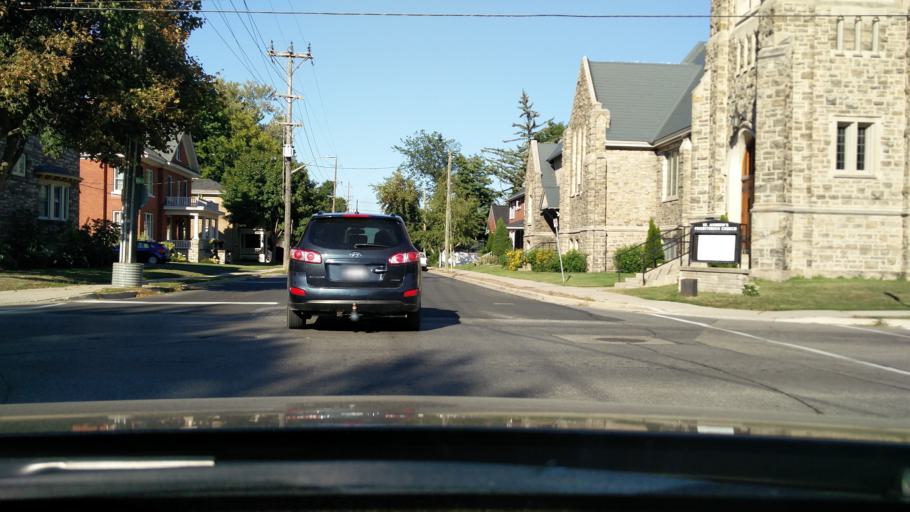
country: CA
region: Ontario
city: Perth
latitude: 44.9025
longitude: -76.2503
